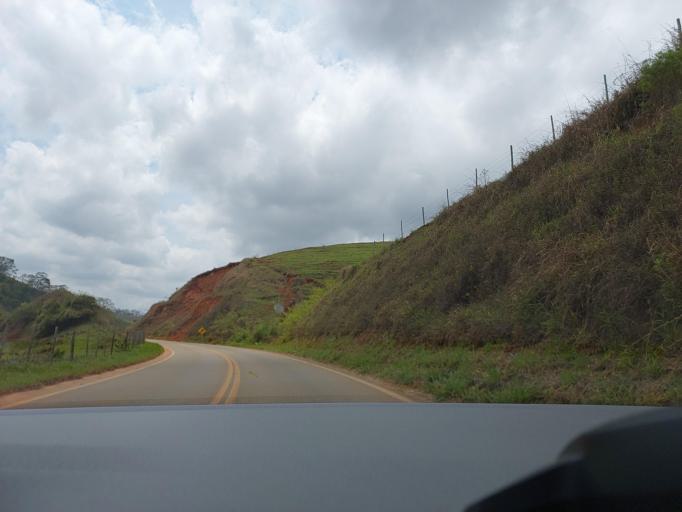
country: BR
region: Minas Gerais
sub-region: Ponte Nova
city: Ponte Nova
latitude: -20.3836
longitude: -42.8889
